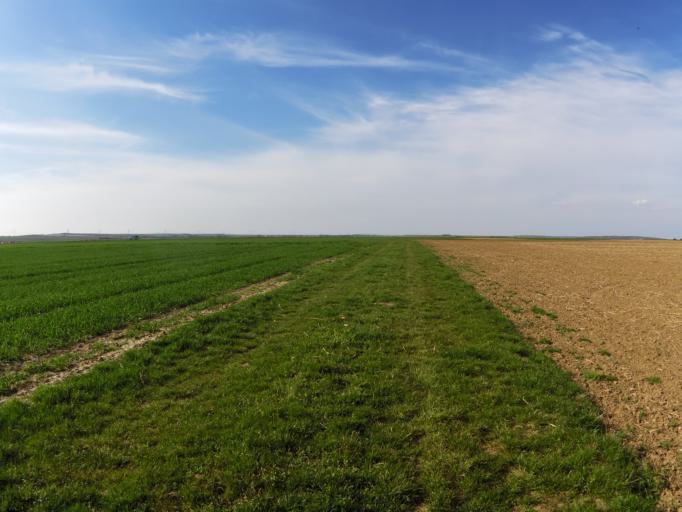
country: DE
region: Bavaria
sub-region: Regierungsbezirk Unterfranken
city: Mainstockheim
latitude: 49.7922
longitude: 10.1269
